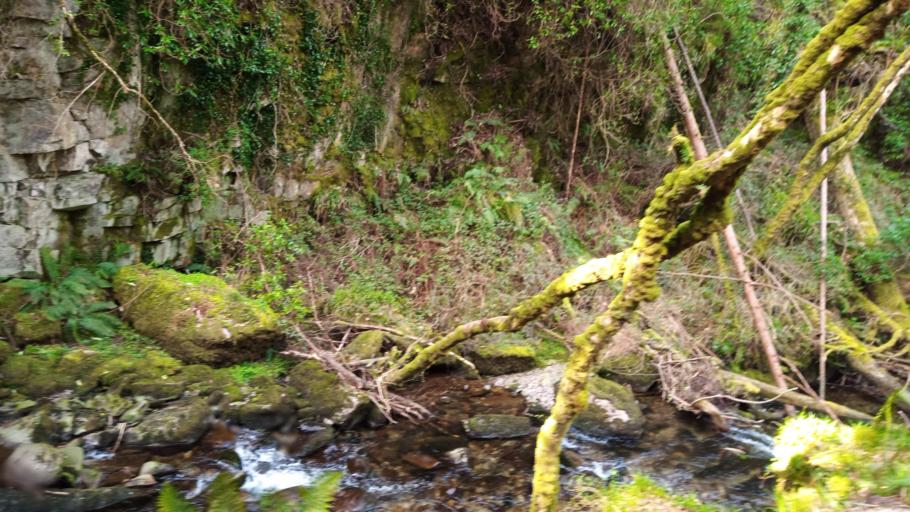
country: IE
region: Munster
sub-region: Ciarrai
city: Cill Airne
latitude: 52.0042
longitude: -9.5064
